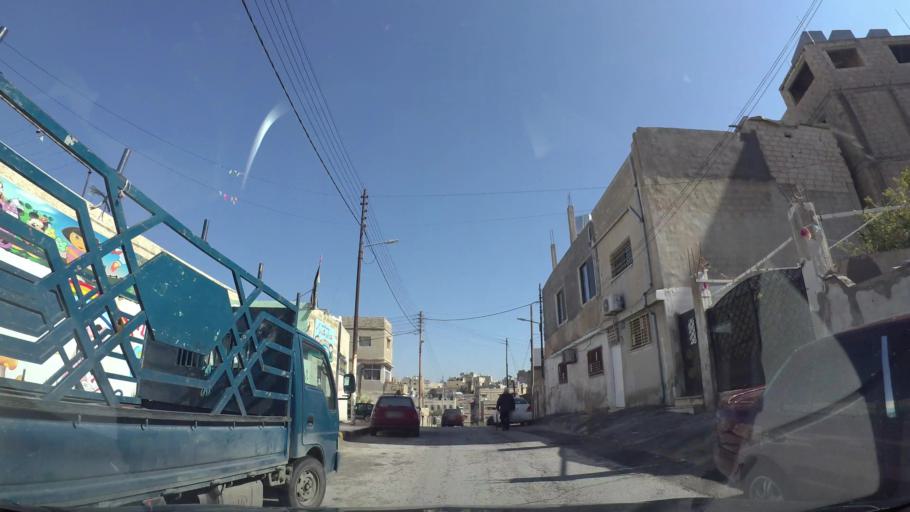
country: JO
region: Amman
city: Amman
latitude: 31.9865
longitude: 35.9878
